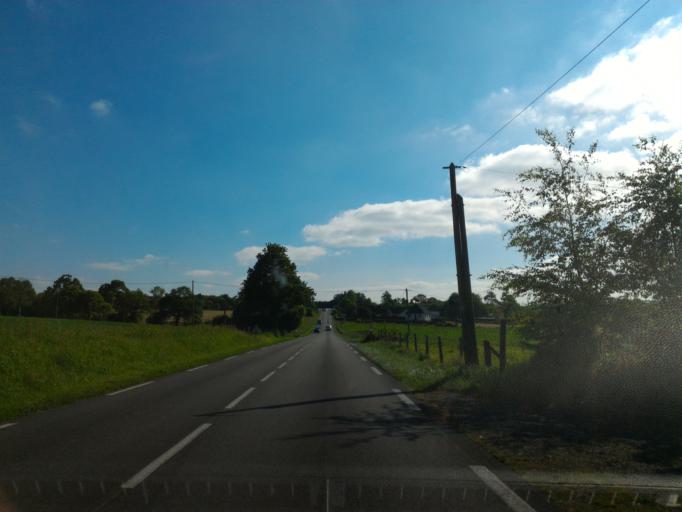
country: FR
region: Lower Normandy
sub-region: Departement de la Manche
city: Villedieu-les-Poeles
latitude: 48.8649
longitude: -1.2030
